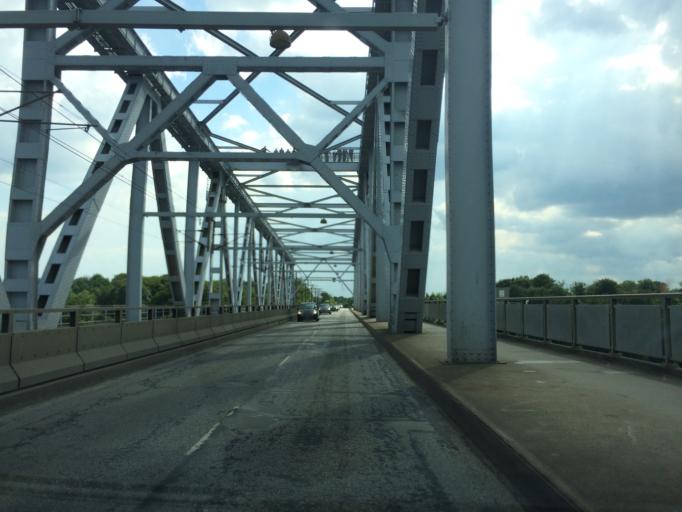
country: DK
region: South Denmark
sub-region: Fredericia Kommune
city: Snoghoj
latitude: 55.5156
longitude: 9.7074
